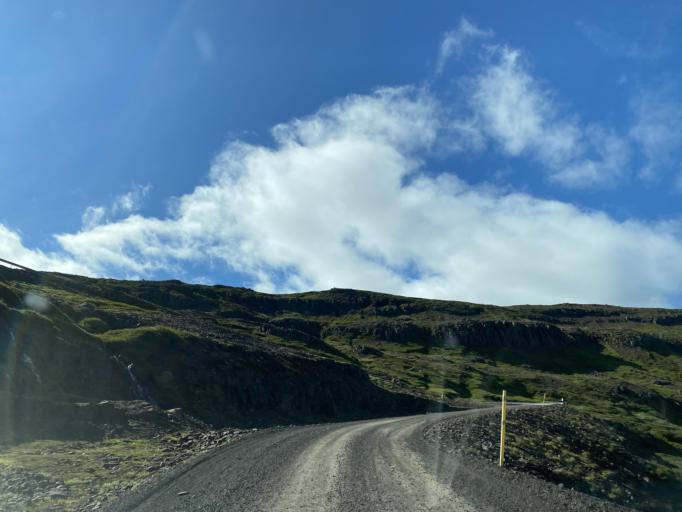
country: IS
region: East
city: Eskifjoerdur
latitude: 65.1797
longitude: -14.0858
